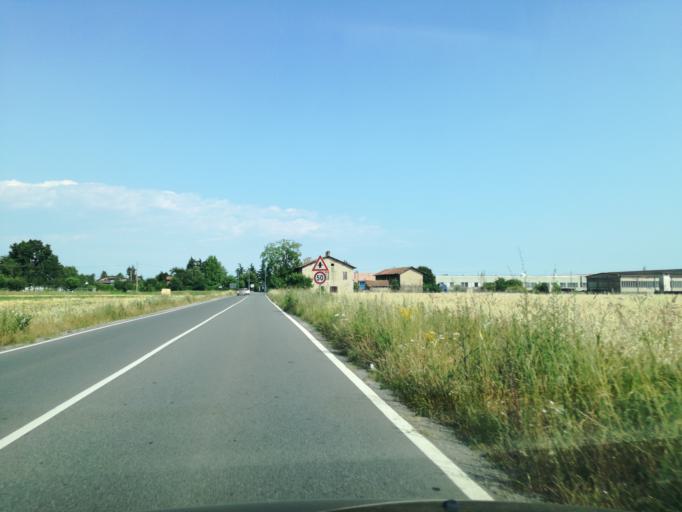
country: IT
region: Lombardy
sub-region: Provincia di Lecco
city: Cernusco Lombardone
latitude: 45.6842
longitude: 9.4054
